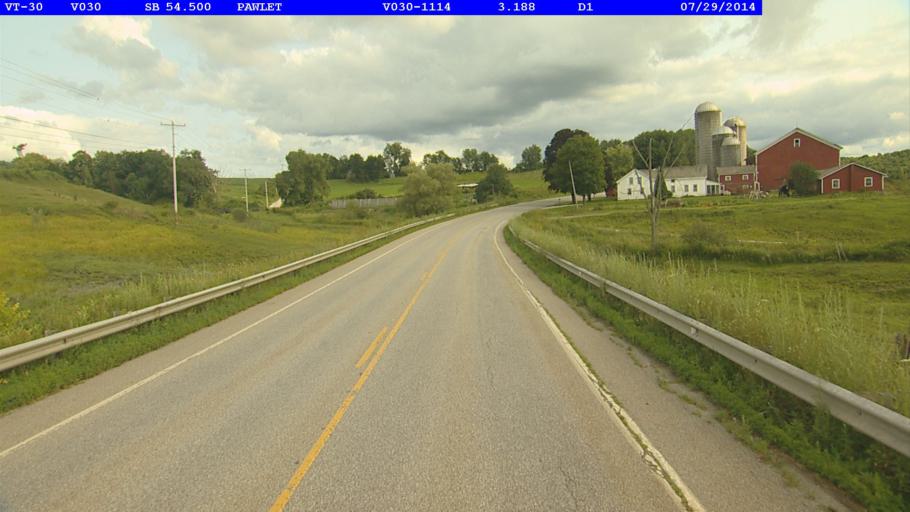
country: US
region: New York
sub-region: Washington County
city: Granville
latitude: 43.3533
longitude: -73.1822
